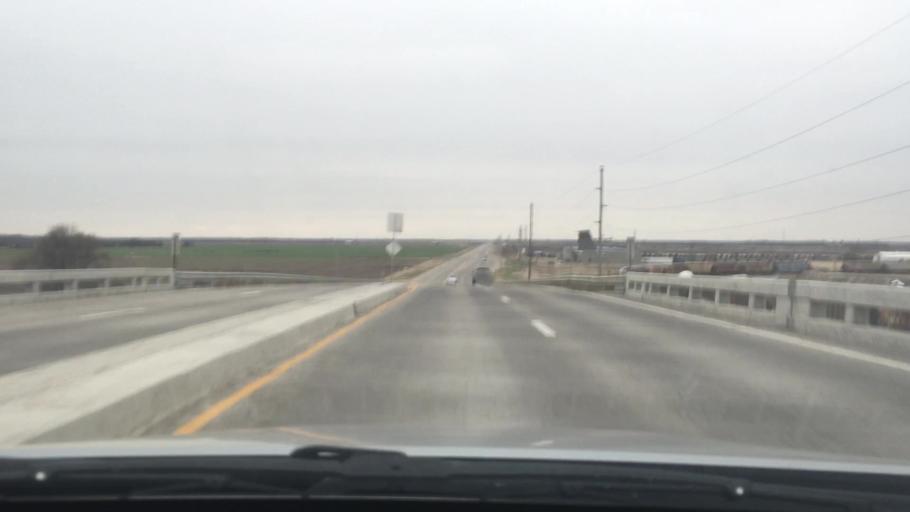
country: US
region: Kansas
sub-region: Reno County
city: Hutchinson
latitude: 38.0478
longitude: -97.8670
